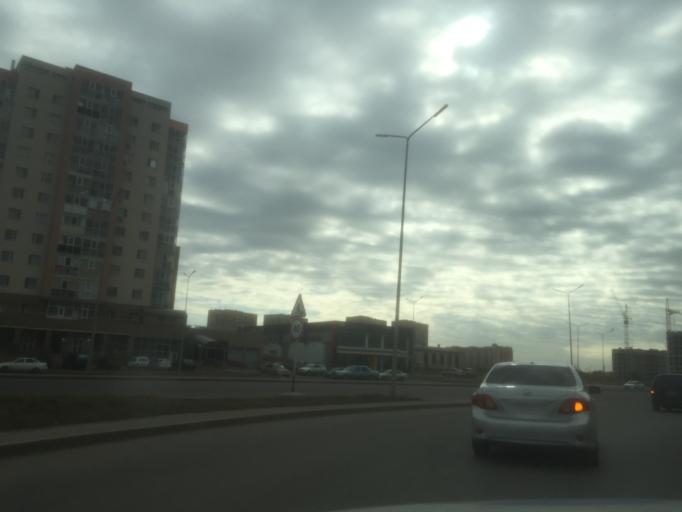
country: KZ
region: Astana Qalasy
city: Astana
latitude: 51.1717
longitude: 71.3766
